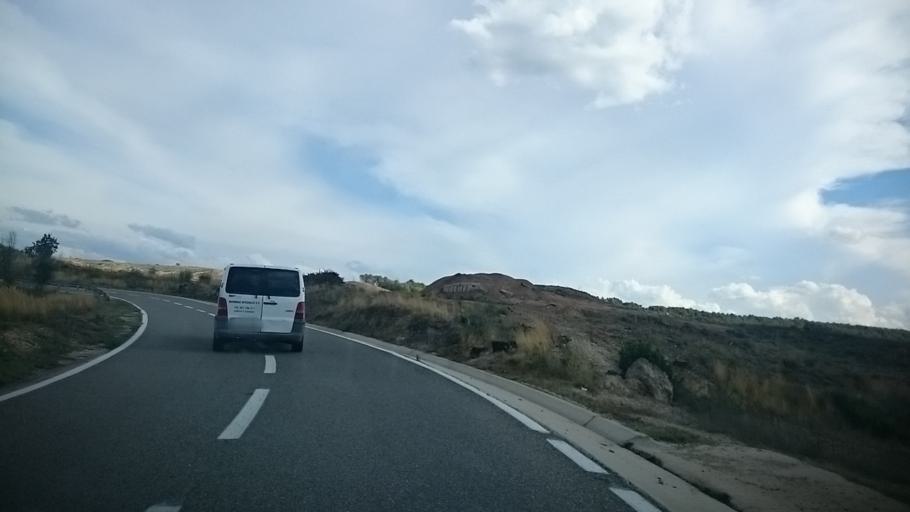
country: ES
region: Catalonia
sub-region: Provincia de Barcelona
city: Odena
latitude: 41.6270
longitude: 1.6744
